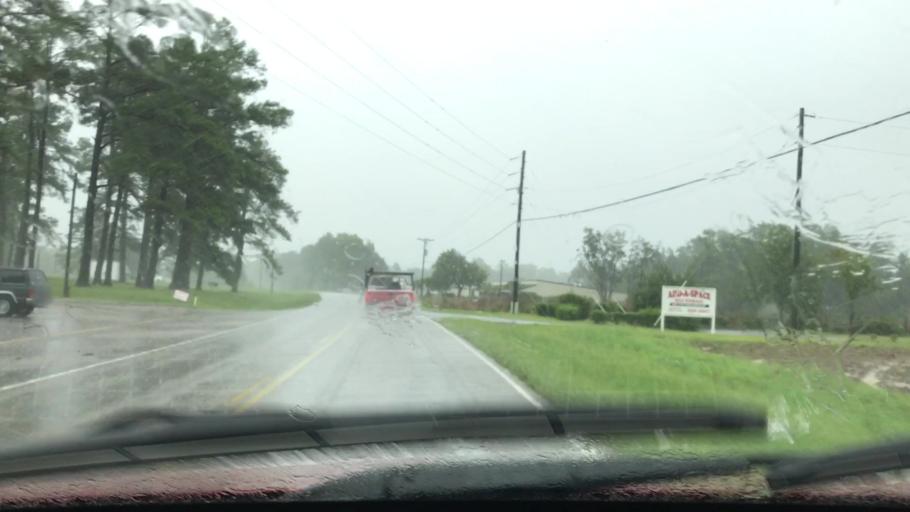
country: US
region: South Carolina
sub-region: Horry County
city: Red Hill
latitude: 33.8632
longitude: -78.9911
